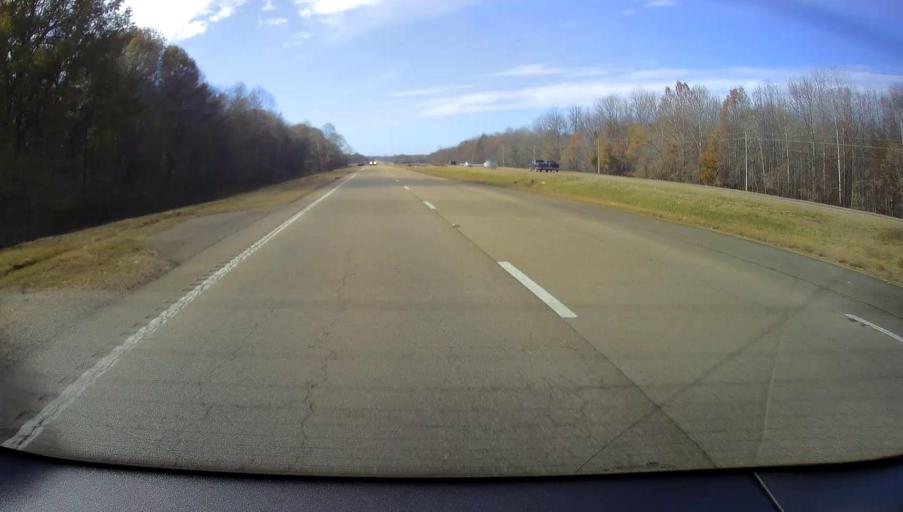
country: US
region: Mississippi
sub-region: Alcorn County
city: Corinth
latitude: 34.9310
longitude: -88.5938
